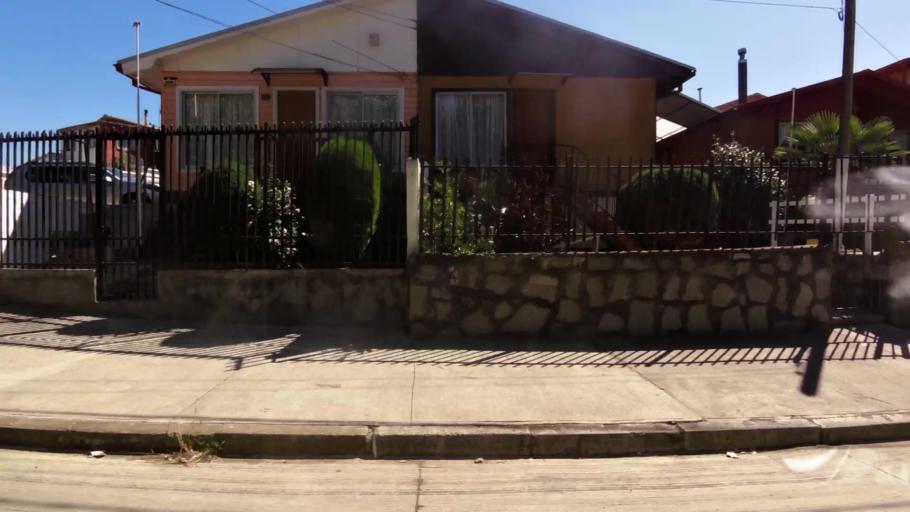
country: CL
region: Biobio
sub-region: Provincia de Concepcion
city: Penco
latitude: -36.7250
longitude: -72.9832
